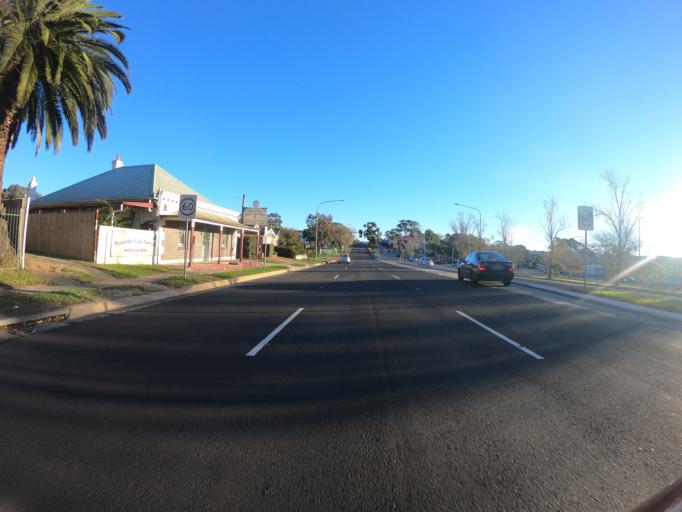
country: AU
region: New South Wales
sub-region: Campbelltown Municipality
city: Campbelltown
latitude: -34.0686
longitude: 150.8153
